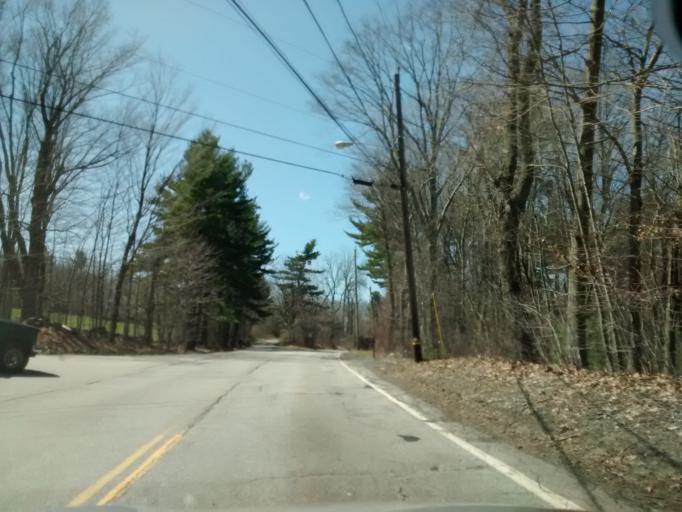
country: US
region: Massachusetts
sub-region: Worcester County
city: Oxford
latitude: 42.1093
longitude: -71.8120
